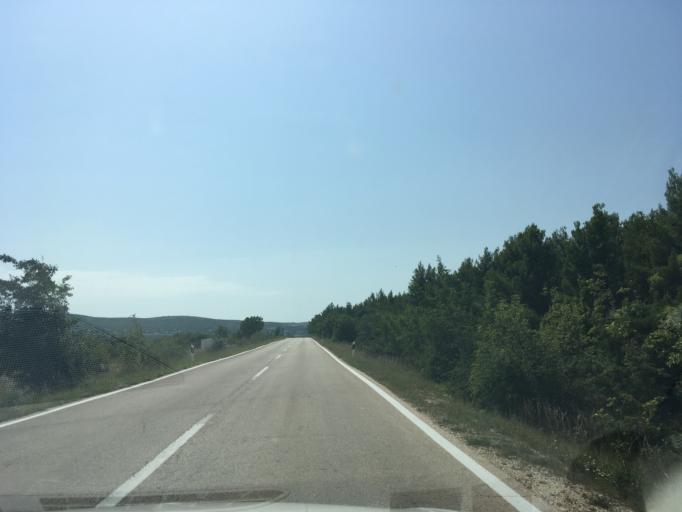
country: HR
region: Zadarska
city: Benkovac
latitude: 43.9653
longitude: 15.7364
